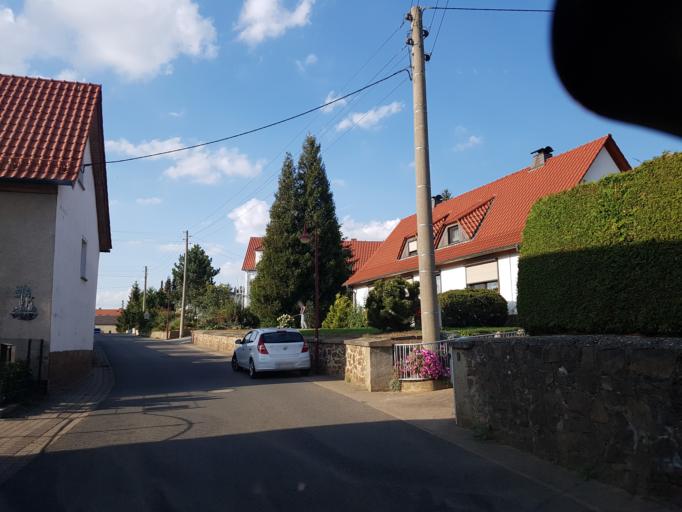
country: DE
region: Saxony
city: Ostrau
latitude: 51.1899
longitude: 13.1410
